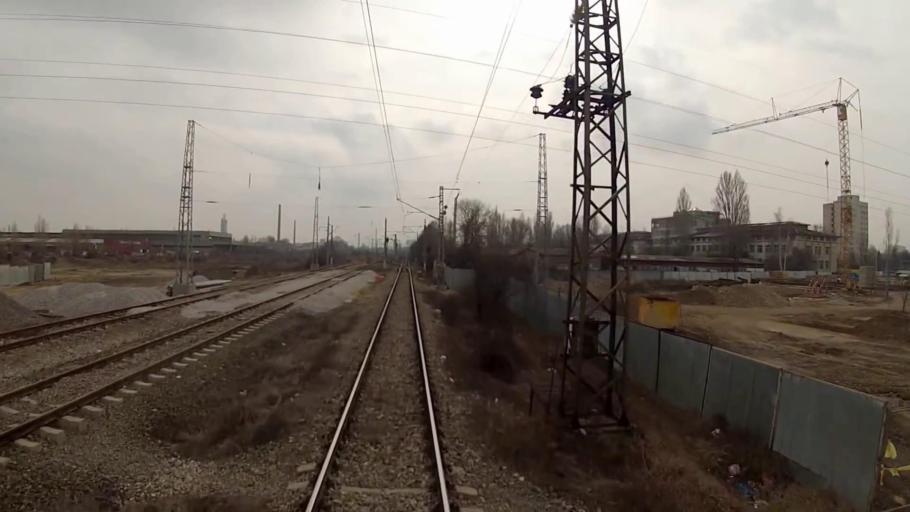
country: BG
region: Sofia-Capital
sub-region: Stolichna Obshtina
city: Sofia
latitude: 42.6623
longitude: 23.4235
